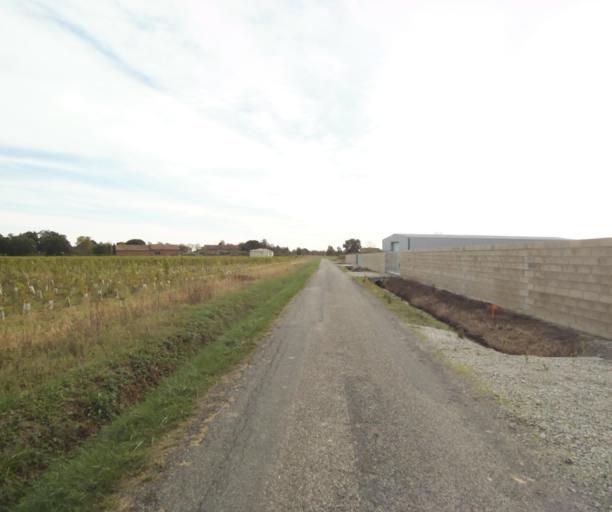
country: FR
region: Midi-Pyrenees
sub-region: Departement de la Haute-Garonne
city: Fronton
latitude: 43.8720
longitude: 1.3844
